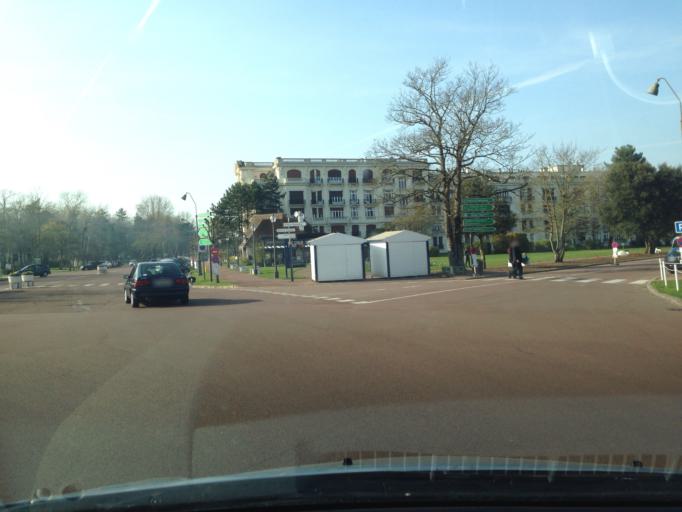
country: FR
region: Nord-Pas-de-Calais
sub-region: Departement du Pas-de-Calais
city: Le Touquet-Paris-Plage
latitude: 50.5185
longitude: 1.5952
